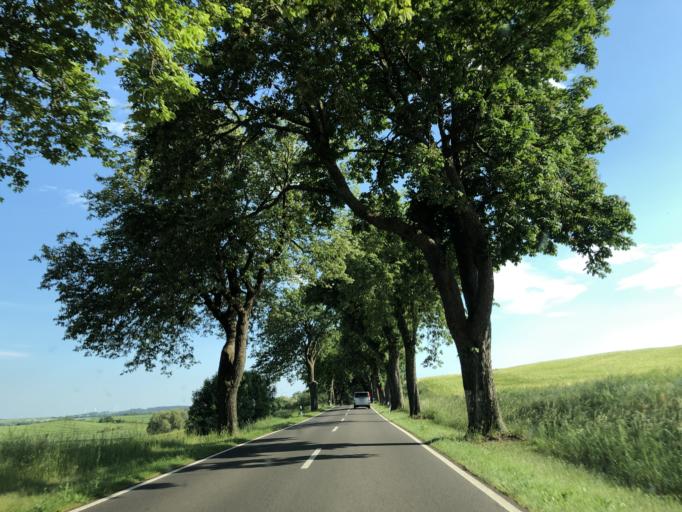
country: DE
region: Brandenburg
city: Angermunde
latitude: 53.1128
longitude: 13.9635
